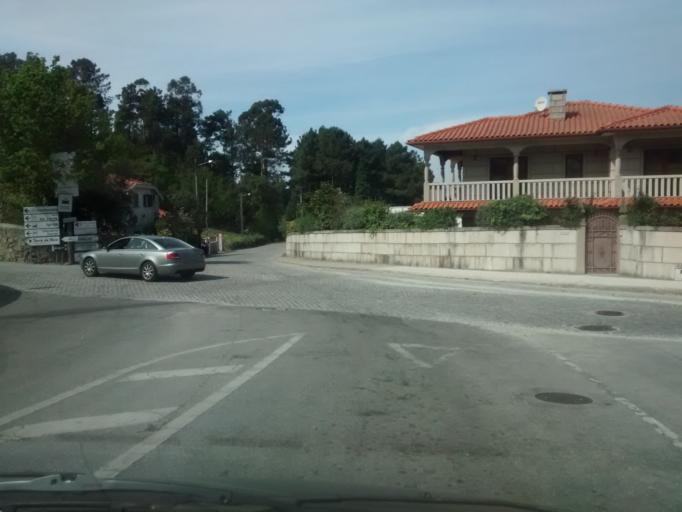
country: PT
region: Braga
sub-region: Braga
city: Braga
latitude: 41.5438
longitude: -8.4427
